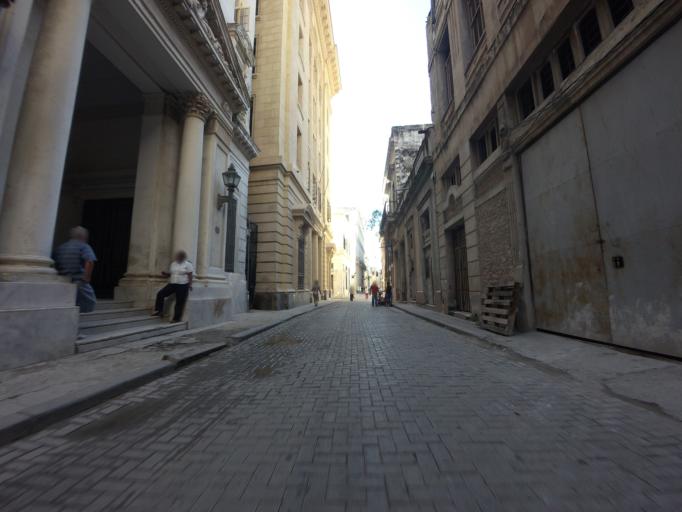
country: CU
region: La Habana
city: La Habana Vieja
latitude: 23.1386
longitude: -82.3529
